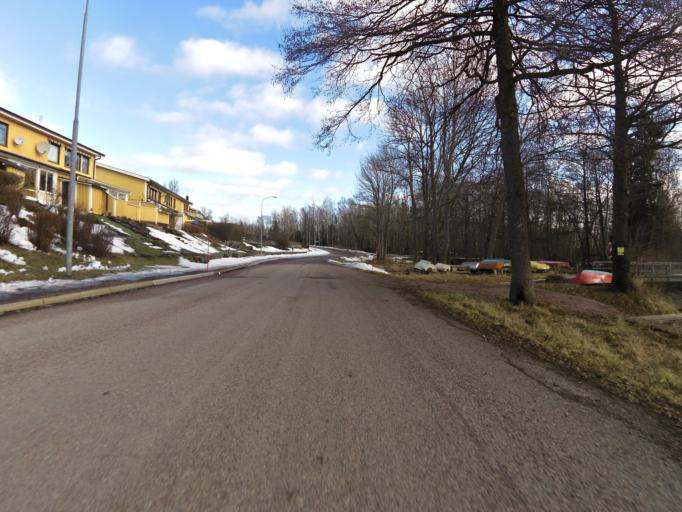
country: SE
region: Uppsala
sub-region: Alvkarleby Kommun
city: Skutskaer
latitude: 60.6494
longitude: 17.3715
